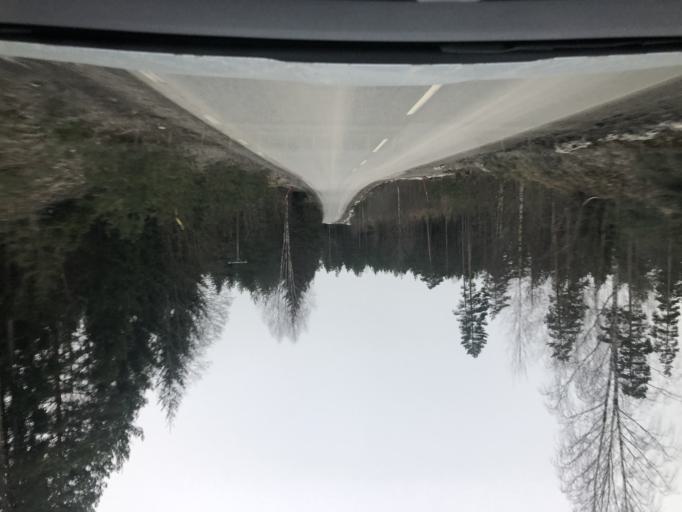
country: SE
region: Stockholm
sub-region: Botkyrka Kommun
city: Tullinge
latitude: 59.1695
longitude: 17.9150
